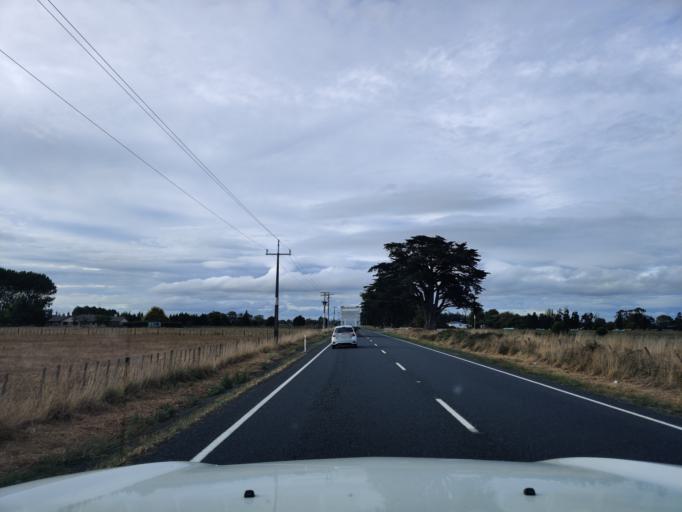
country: NZ
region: Waikato
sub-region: Hamilton City
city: Hamilton
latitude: -37.6999
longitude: 175.3381
